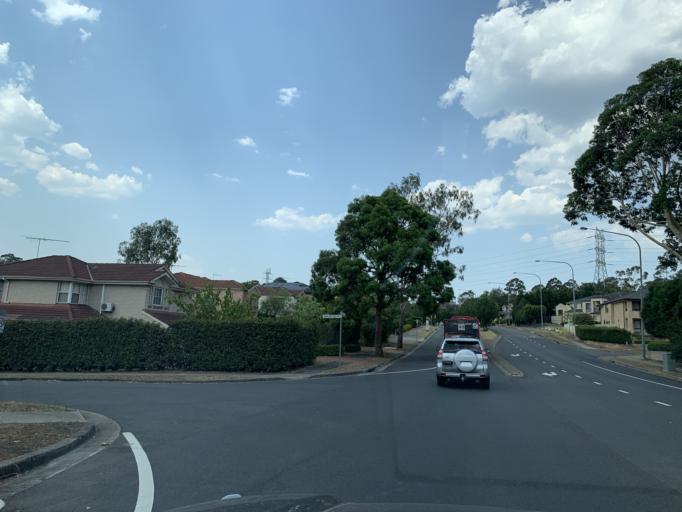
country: AU
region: New South Wales
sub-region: The Hills Shire
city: West Pennant
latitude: -33.7261
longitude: 151.0353
